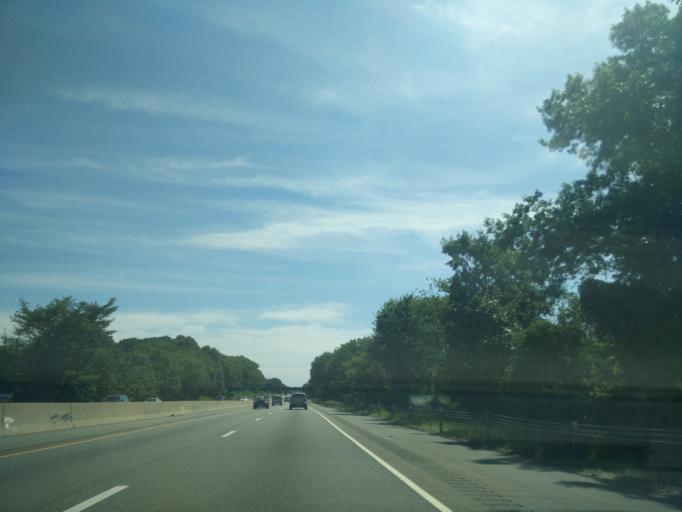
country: US
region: Connecticut
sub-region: New Haven County
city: Guilford Center
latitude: 41.2885
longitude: -72.6434
